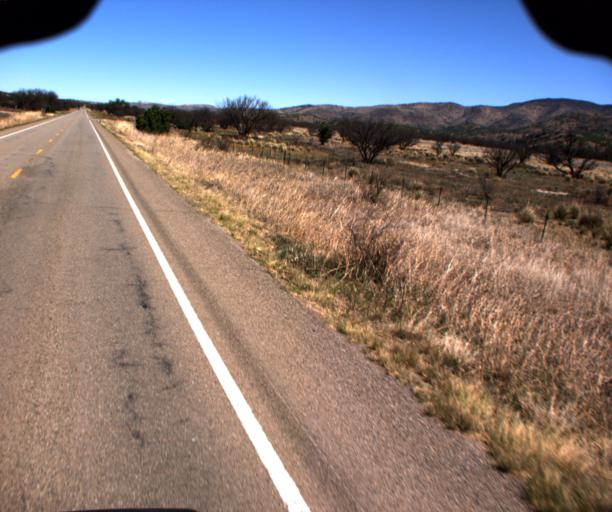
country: US
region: Arizona
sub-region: Santa Cruz County
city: Rio Rico
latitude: 31.5719
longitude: -110.7300
